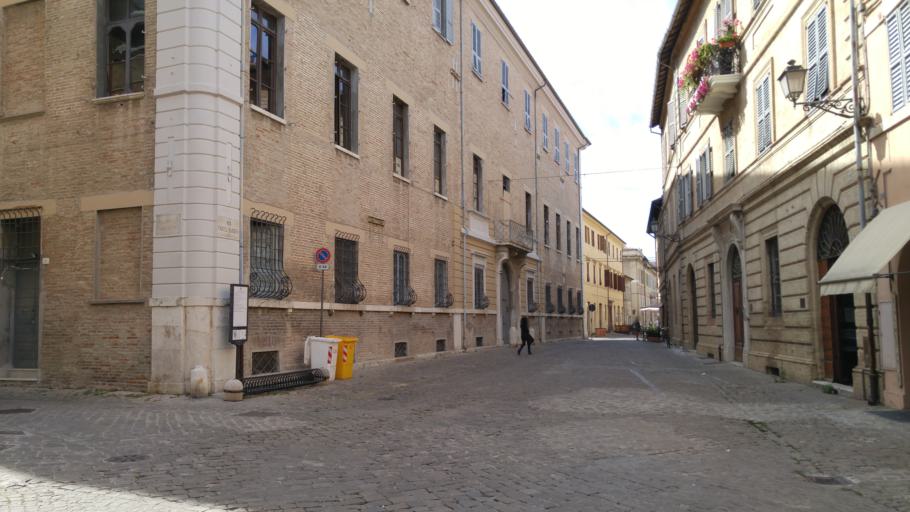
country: IT
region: The Marches
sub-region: Provincia di Ancona
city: Senigallia
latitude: 43.7129
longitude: 13.2181
